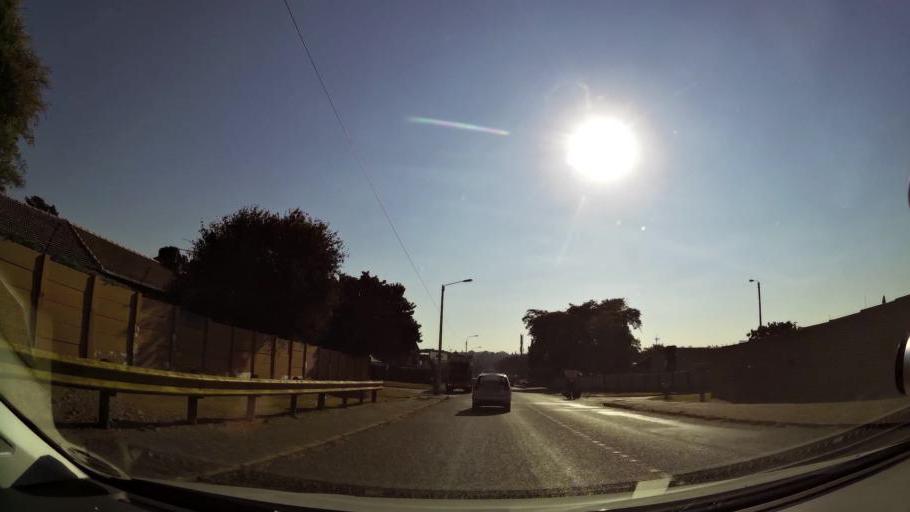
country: ZA
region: Gauteng
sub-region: City of Johannesburg Metropolitan Municipality
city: Modderfontein
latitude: -26.1375
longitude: 28.1601
